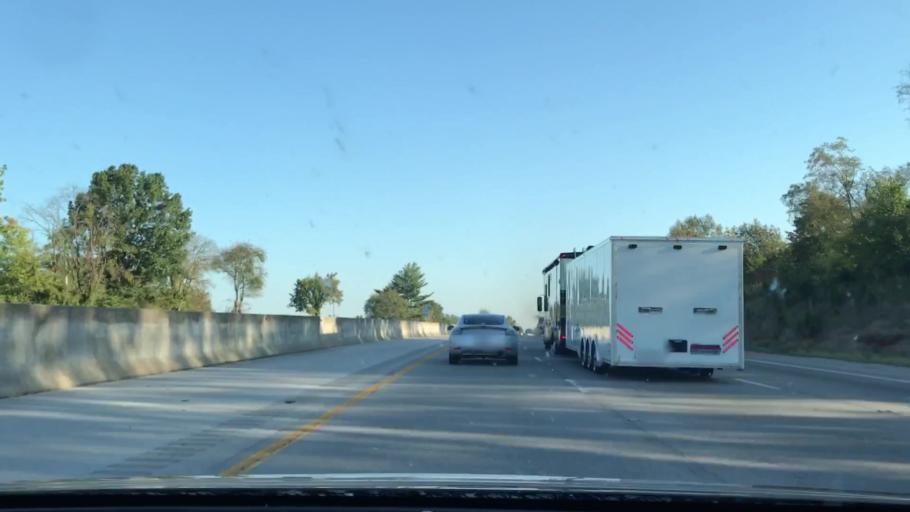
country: US
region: Kentucky
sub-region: Warren County
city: Plano
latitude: 36.8145
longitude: -86.4733
